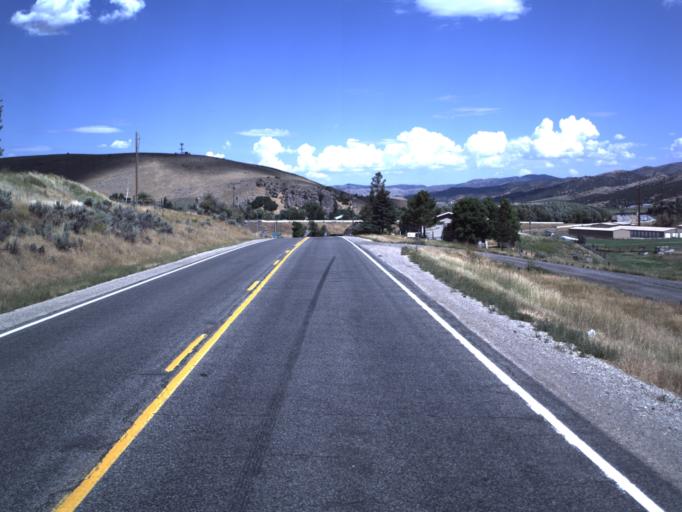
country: US
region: Utah
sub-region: Summit County
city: Coalville
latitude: 40.8044
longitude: -111.4082
